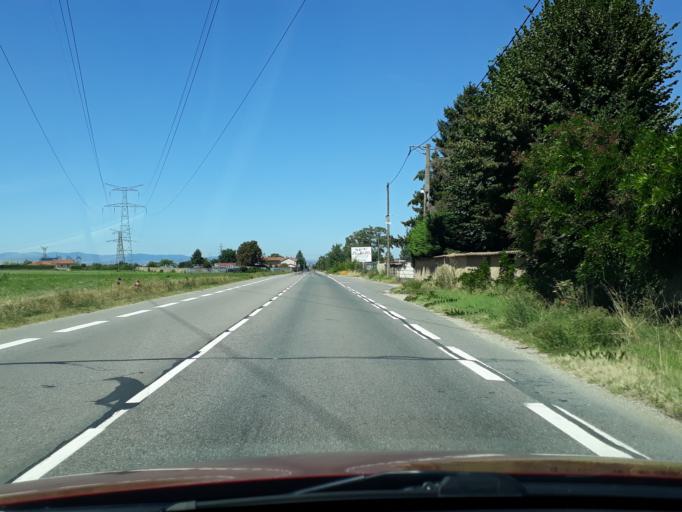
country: FR
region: Rhone-Alpes
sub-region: Departement du Rhone
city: Toussieu
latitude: 45.6672
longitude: 4.9881
